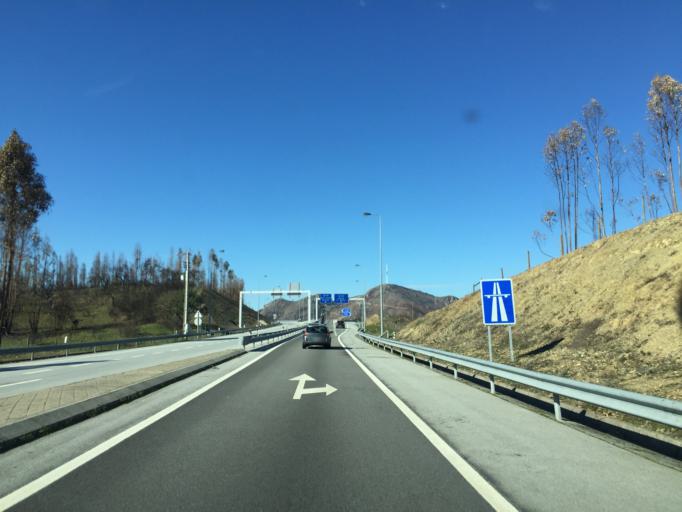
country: PT
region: Portalegre
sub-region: Nisa
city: Nisa
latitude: 39.5570
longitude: -7.7973
